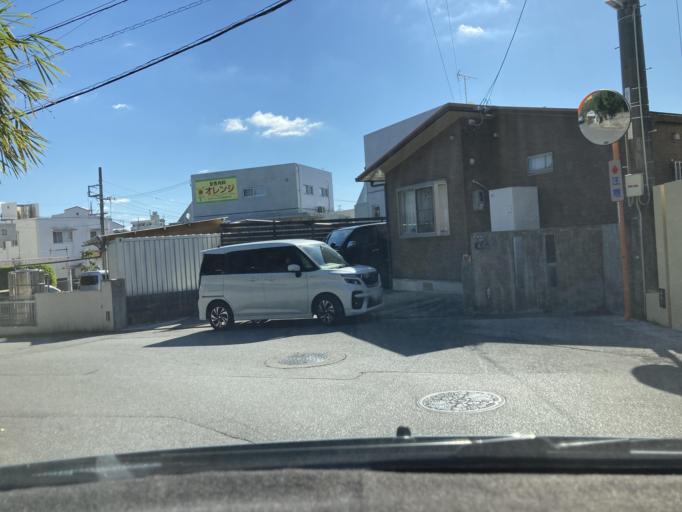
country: JP
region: Okinawa
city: Okinawa
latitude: 26.3442
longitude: 127.8294
